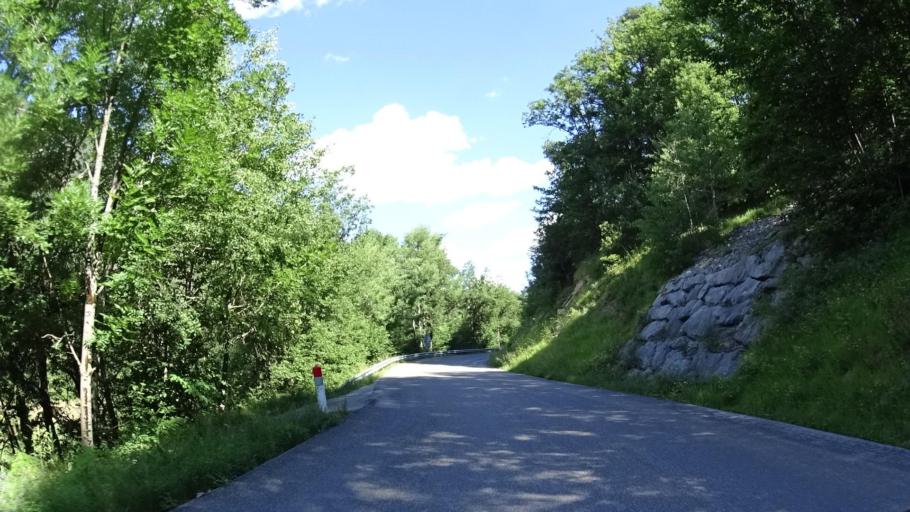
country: FR
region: Provence-Alpes-Cote d'Azur
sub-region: Departement des Alpes-de-Haute-Provence
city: Annot
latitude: 43.9950
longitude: 6.6461
